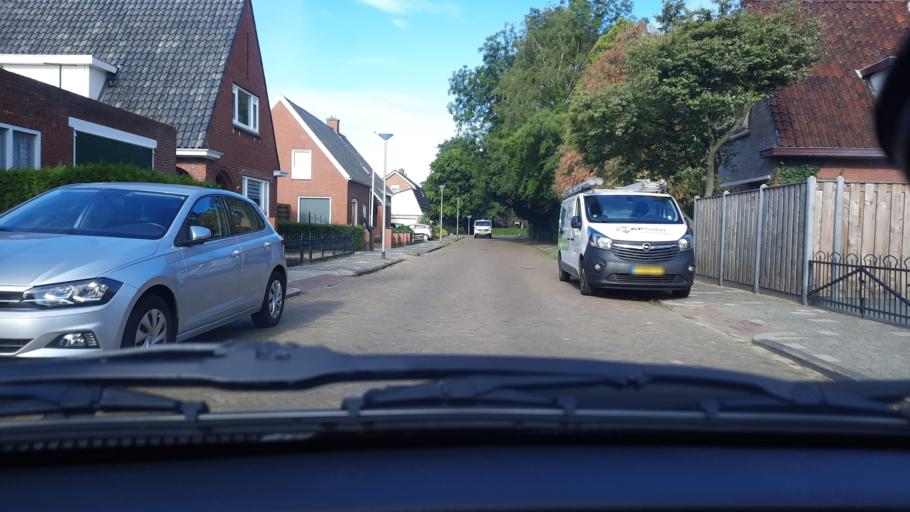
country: NL
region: Groningen
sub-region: Gemeente Hoogezand-Sappemeer
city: Sappemeer
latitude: 53.1614
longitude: 6.7877
